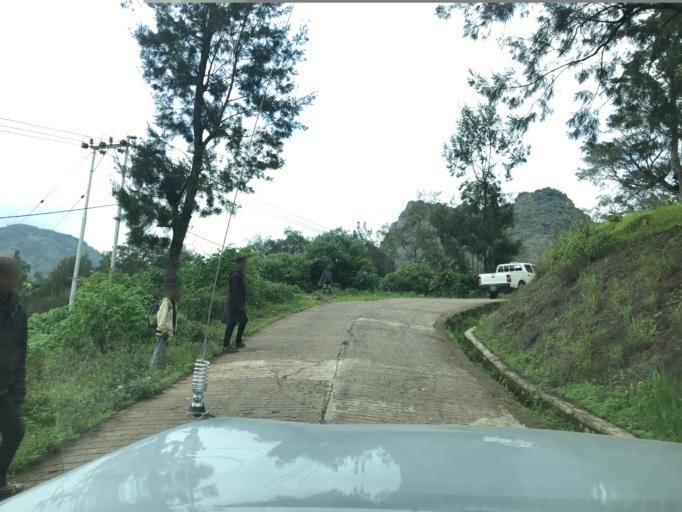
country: TL
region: Aileu
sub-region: Aileu Villa
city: Aileu
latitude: -8.8525
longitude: 125.5837
